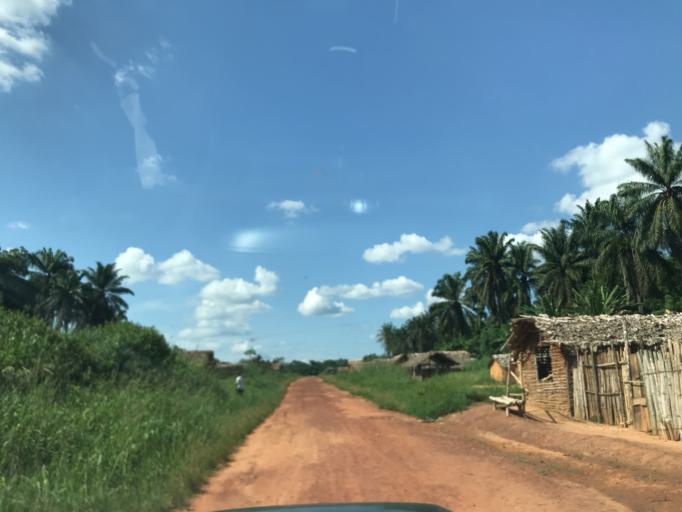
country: CD
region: Eastern Province
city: Kisangani
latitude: 1.2487
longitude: 25.2734
